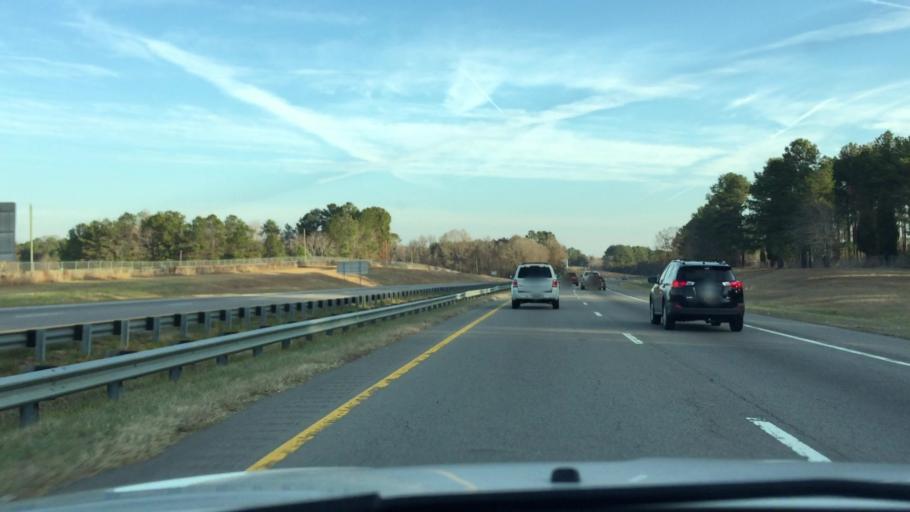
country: US
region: North Carolina
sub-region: Lee County
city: Sanford
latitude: 35.5297
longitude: -79.1815
